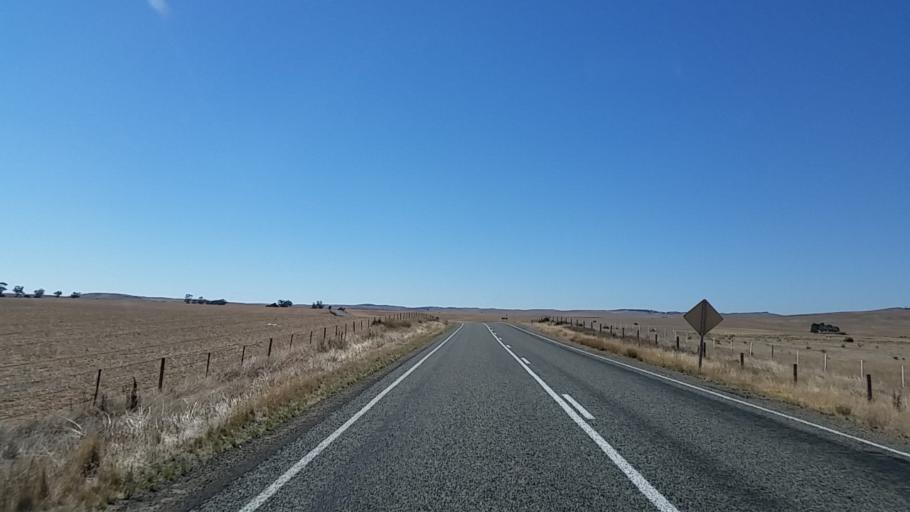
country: AU
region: South Australia
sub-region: Northern Areas
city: Jamestown
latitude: -33.3494
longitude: 138.8906
